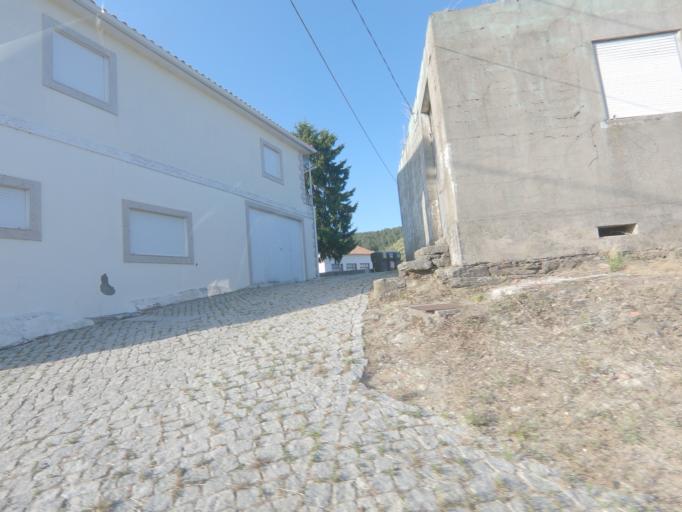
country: PT
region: Vila Real
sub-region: Sabrosa
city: Vilela
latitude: 41.2241
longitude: -7.6024
